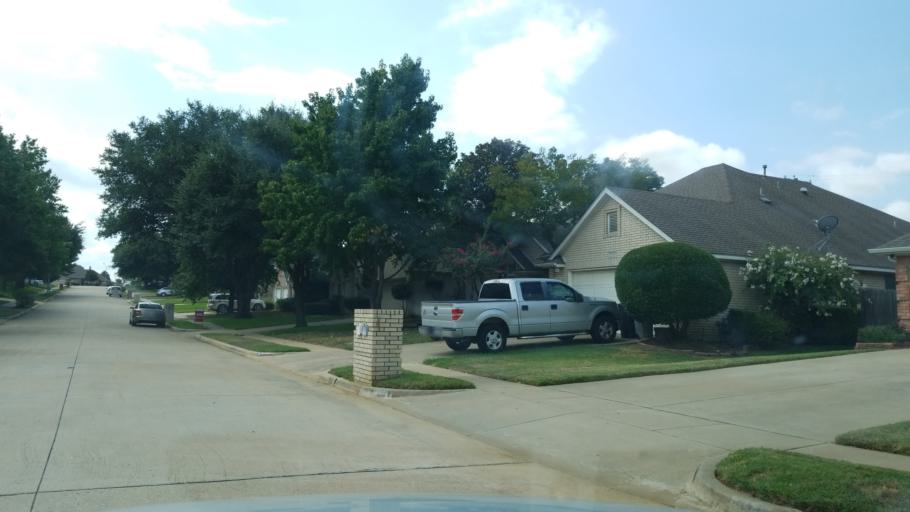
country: US
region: Texas
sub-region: Tarrant County
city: Euless
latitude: 32.8513
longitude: -97.0977
